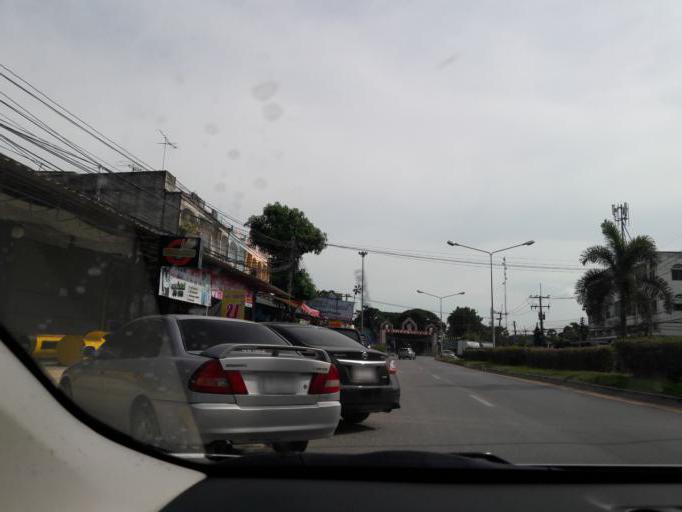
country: TH
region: Ang Thong
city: Ang Thong
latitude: 14.5917
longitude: 100.4455
